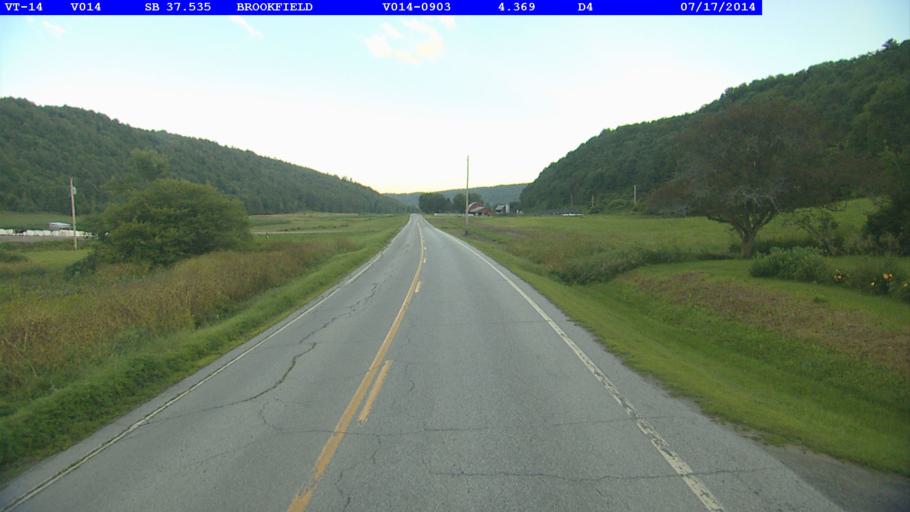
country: US
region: Vermont
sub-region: Orange County
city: Williamstown
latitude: 44.0399
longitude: -72.5692
